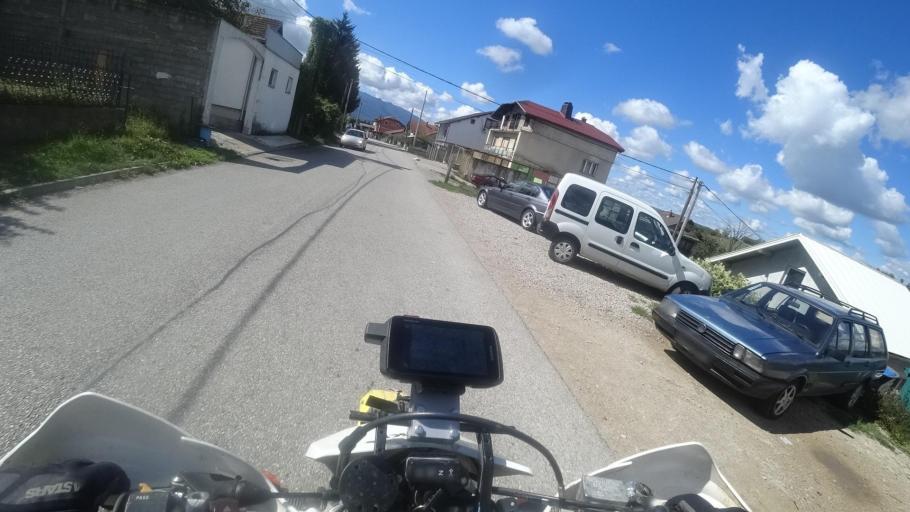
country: BA
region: Federation of Bosnia and Herzegovina
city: Bihac
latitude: 44.8139
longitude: 15.8935
